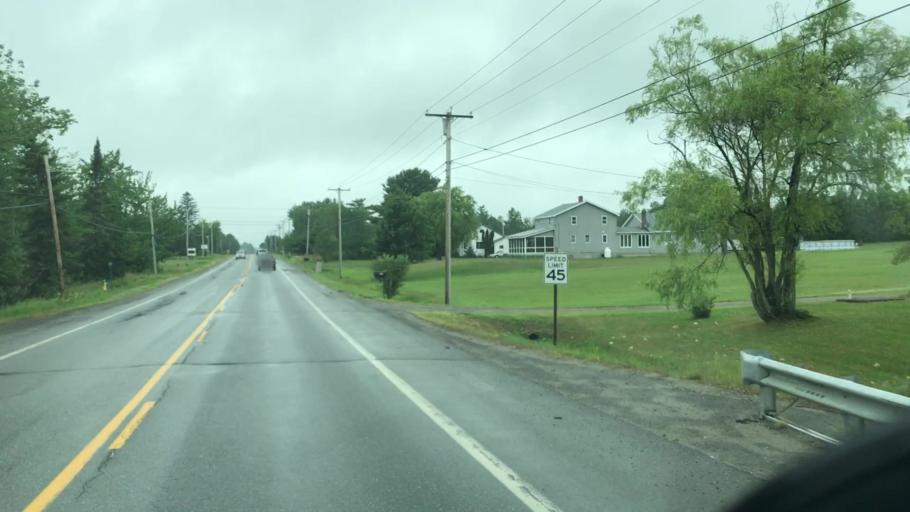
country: US
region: Maine
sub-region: Penobscot County
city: Lincoln
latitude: 45.3519
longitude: -68.5370
